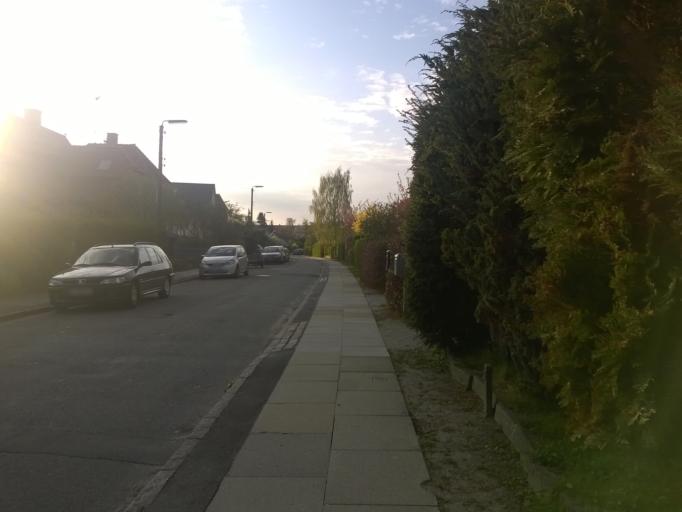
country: DK
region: Capital Region
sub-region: Kobenhavn
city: Vanlose
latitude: 55.6894
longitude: 12.4942
